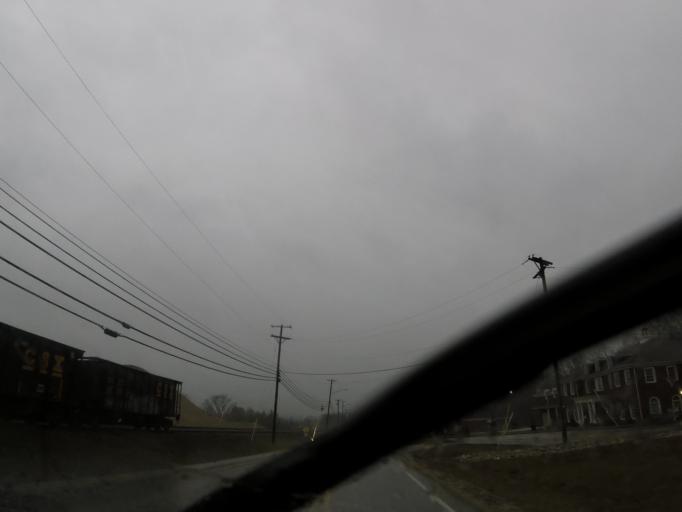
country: US
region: Kentucky
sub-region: Rockcastle County
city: Mount Vernon
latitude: 37.3508
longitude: -84.3496
